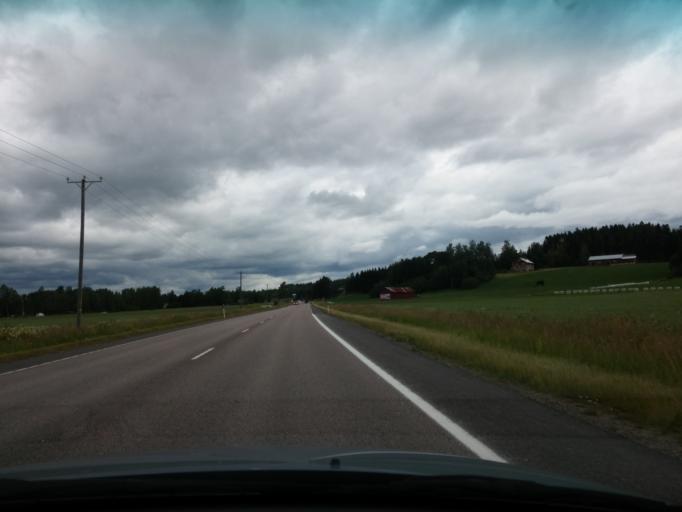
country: FI
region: Uusimaa
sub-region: Porvoo
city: Askola
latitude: 60.4549
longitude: 25.5819
